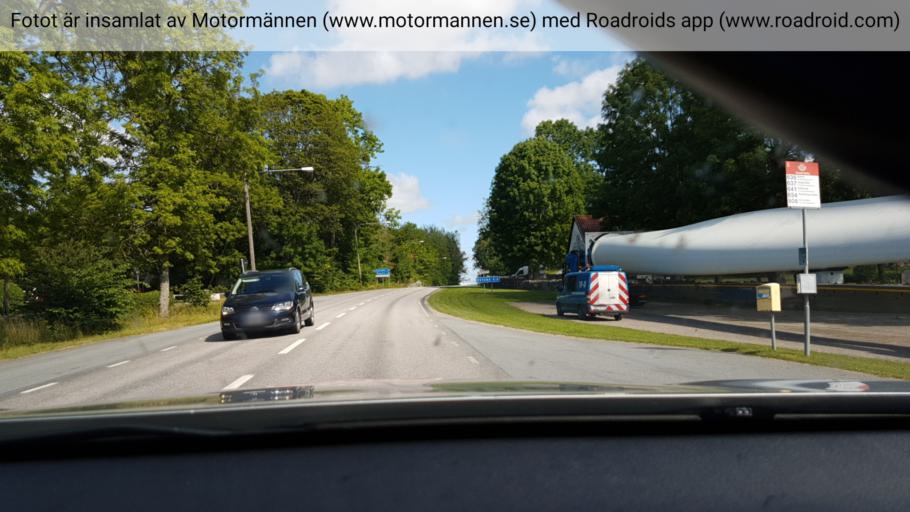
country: SE
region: Stockholm
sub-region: Norrtalje Kommun
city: Norrtalje
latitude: 59.8176
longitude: 18.6510
